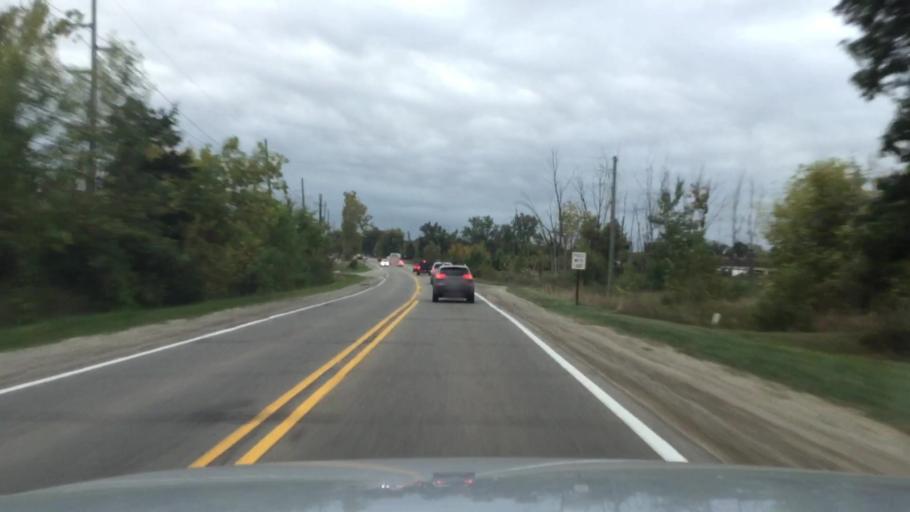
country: US
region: Michigan
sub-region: Livingston County
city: Brighton
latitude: 42.6221
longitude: -83.7518
